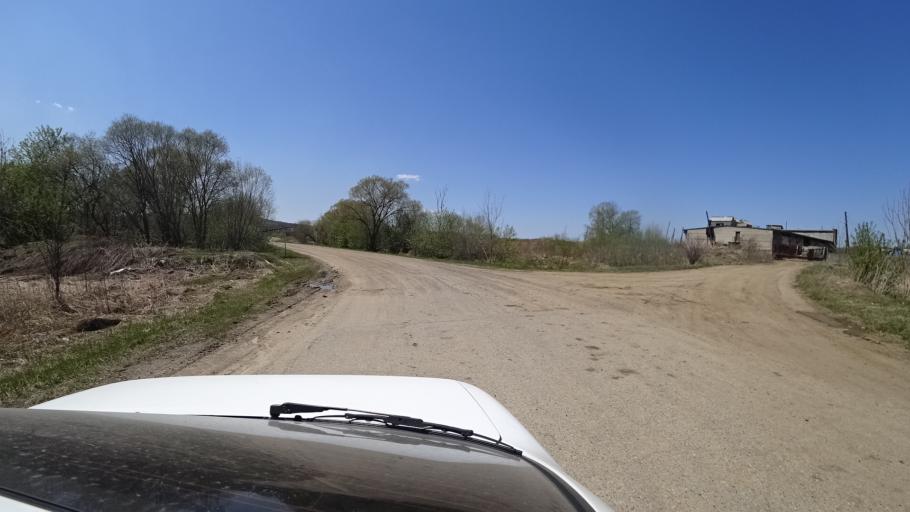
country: RU
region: Primorskiy
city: Lazo
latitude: 45.7960
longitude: 133.7617
